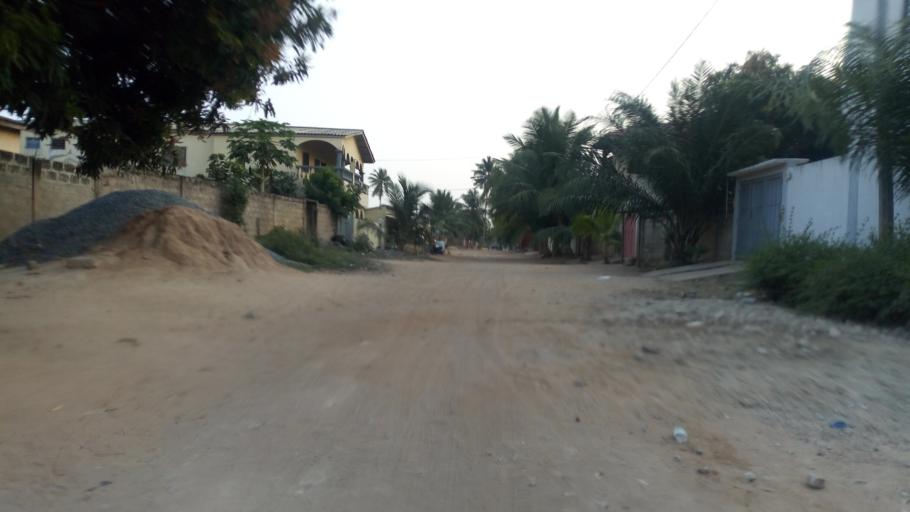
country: TG
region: Maritime
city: Lome
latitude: 6.1898
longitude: 1.1381
